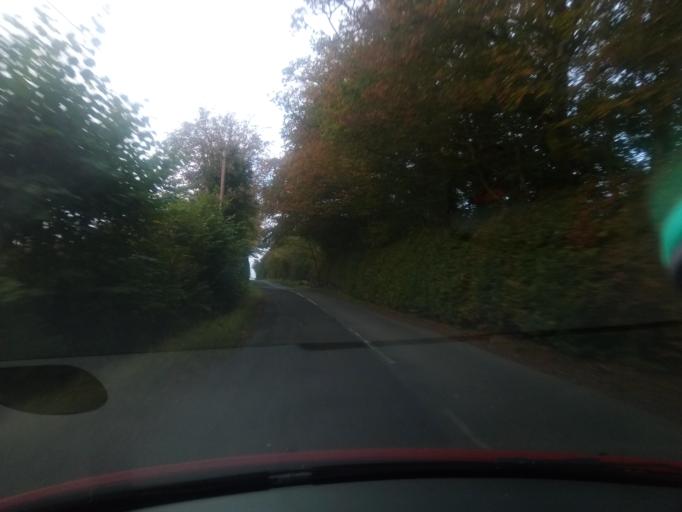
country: GB
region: Scotland
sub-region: The Scottish Borders
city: Jedburgh
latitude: 55.4498
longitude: -2.5703
